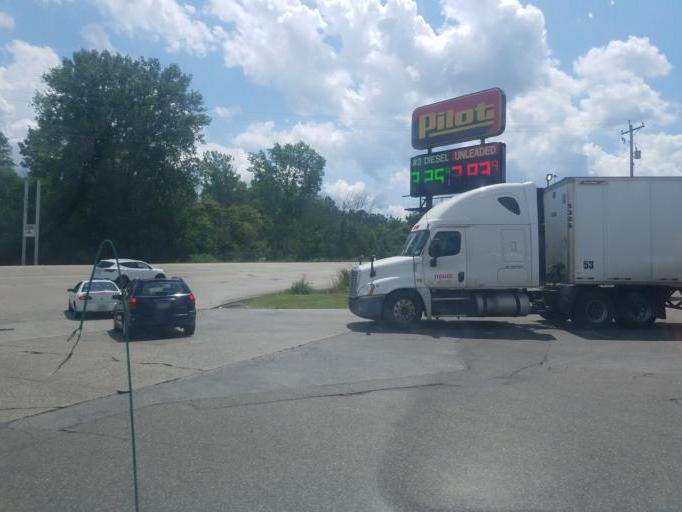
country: US
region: Ohio
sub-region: Fairfield County
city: Millersport
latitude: 39.9455
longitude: -82.5358
